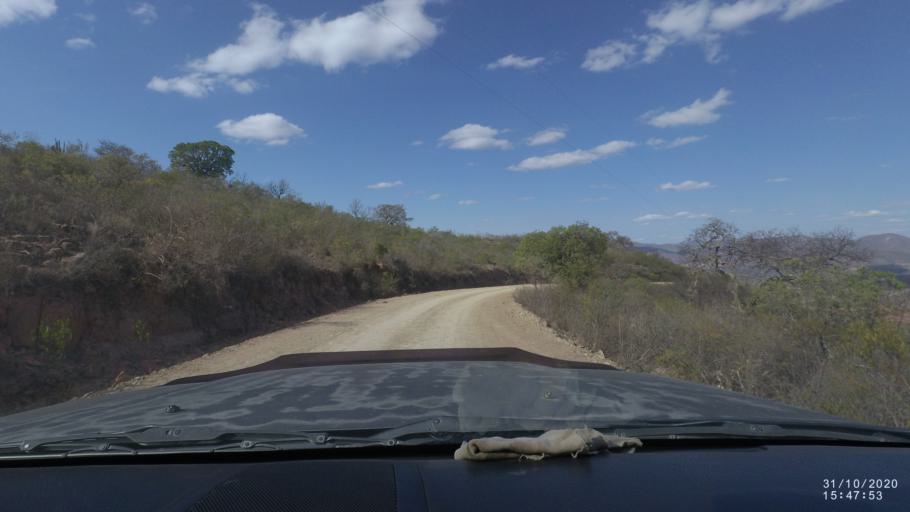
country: BO
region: Chuquisaca
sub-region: Provincia Zudanez
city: Mojocoya
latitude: -18.3142
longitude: -64.7133
